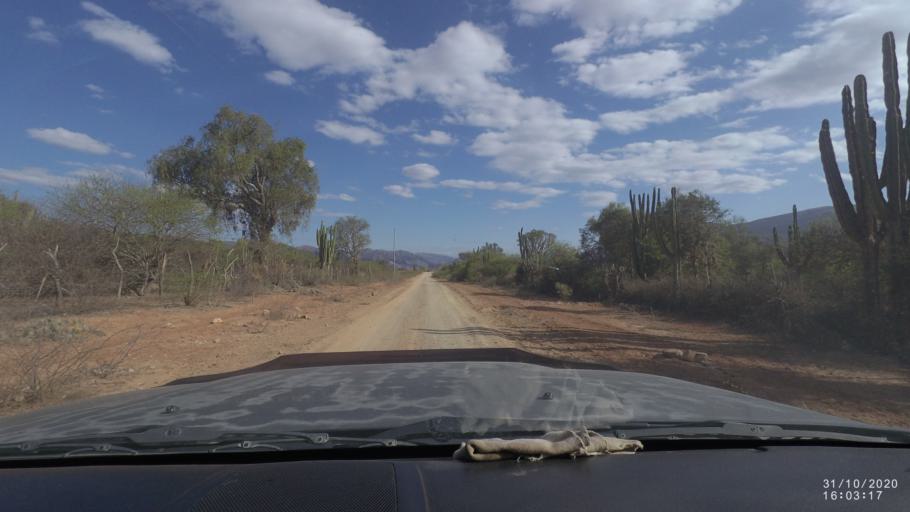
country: BO
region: Chuquisaca
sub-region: Provincia Zudanez
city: Mojocoya
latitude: -18.3506
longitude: -64.6535
